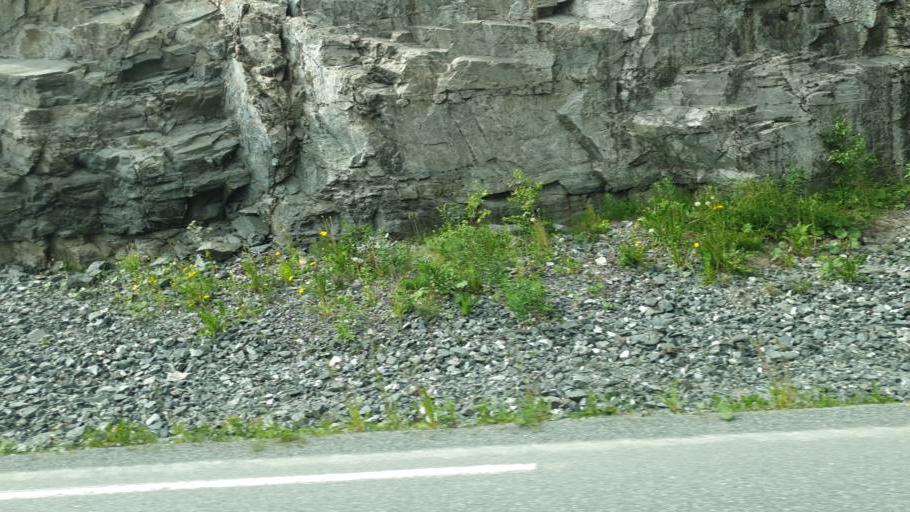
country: NO
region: Sor-Trondelag
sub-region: Trondheim
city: Trondheim
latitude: 63.5988
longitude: 10.4589
